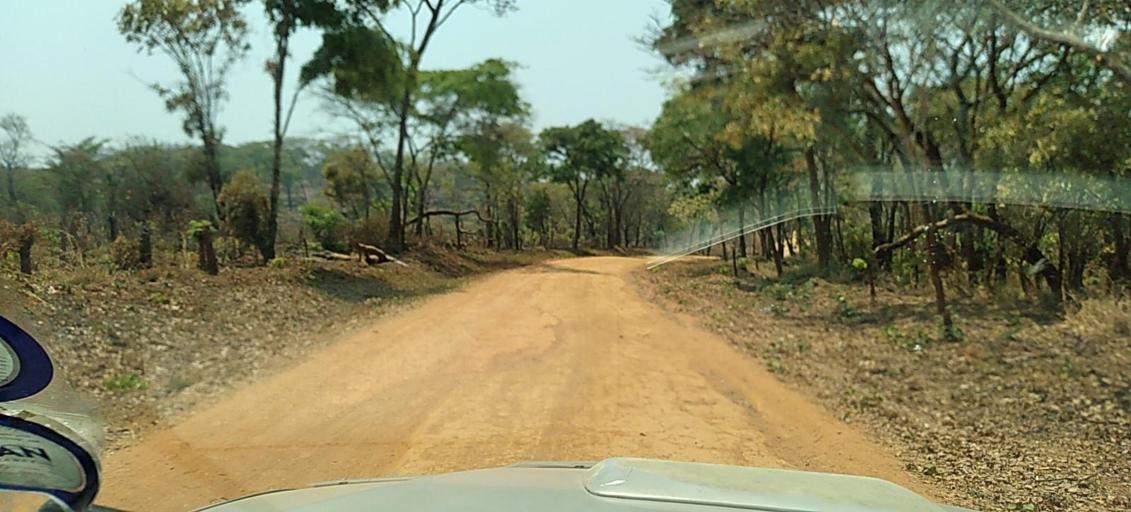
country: ZM
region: North-Western
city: Kasempa
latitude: -13.5451
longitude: 26.0403
